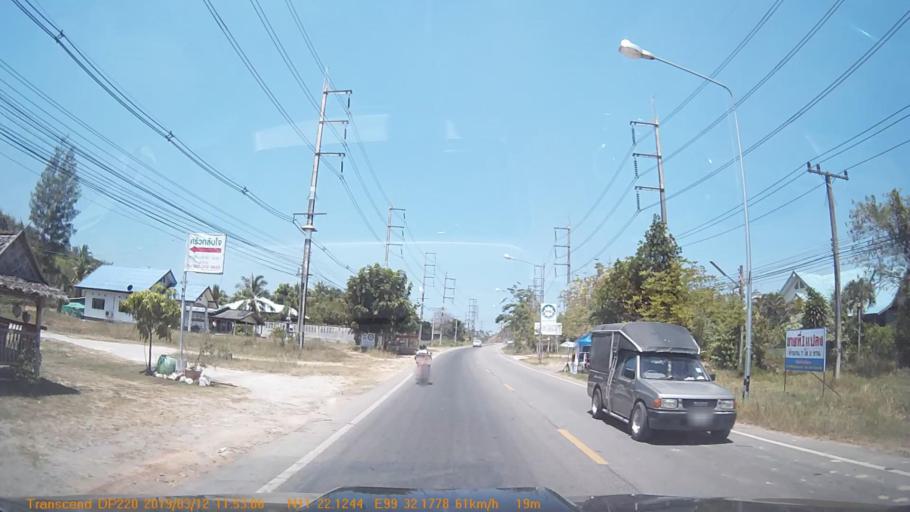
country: TH
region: Prachuap Khiri Khan
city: Thap Sakae
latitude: 11.3688
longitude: 99.5362
